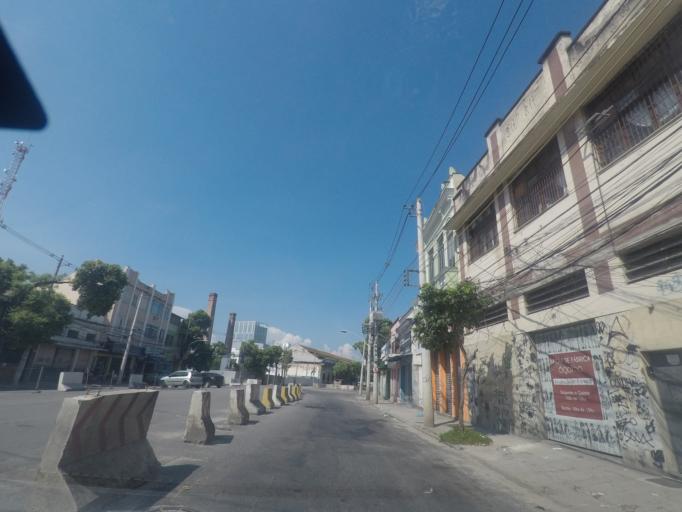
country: BR
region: Rio de Janeiro
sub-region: Rio De Janeiro
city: Rio de Janeiro
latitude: -22.9009
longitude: -43.2164
